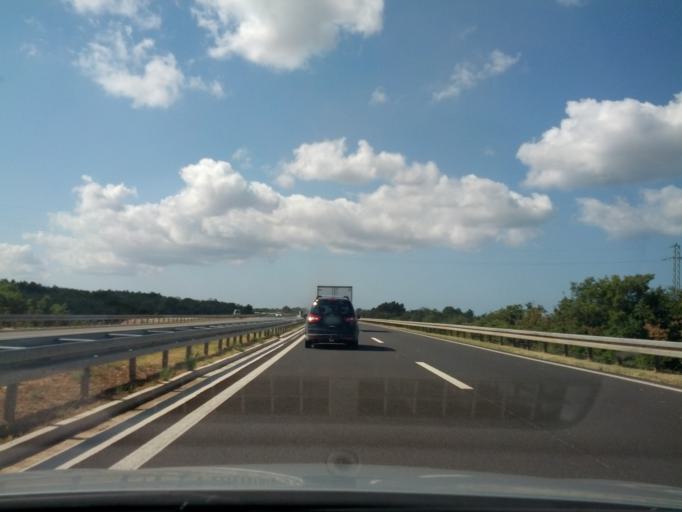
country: HR
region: Istarska
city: Vodnjan
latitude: 45.0102
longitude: 13.8381
